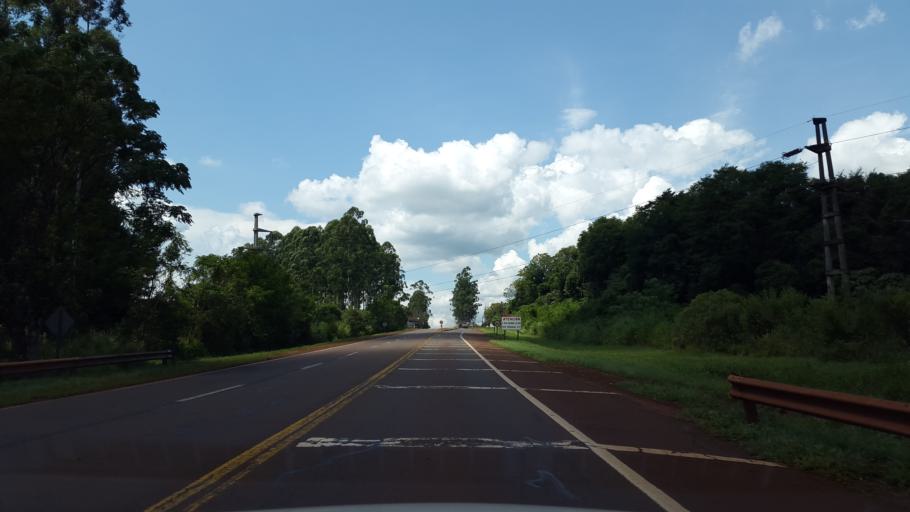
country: AR
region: Misiones
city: El Alcazar
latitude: -26.6914
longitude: -54.8239
